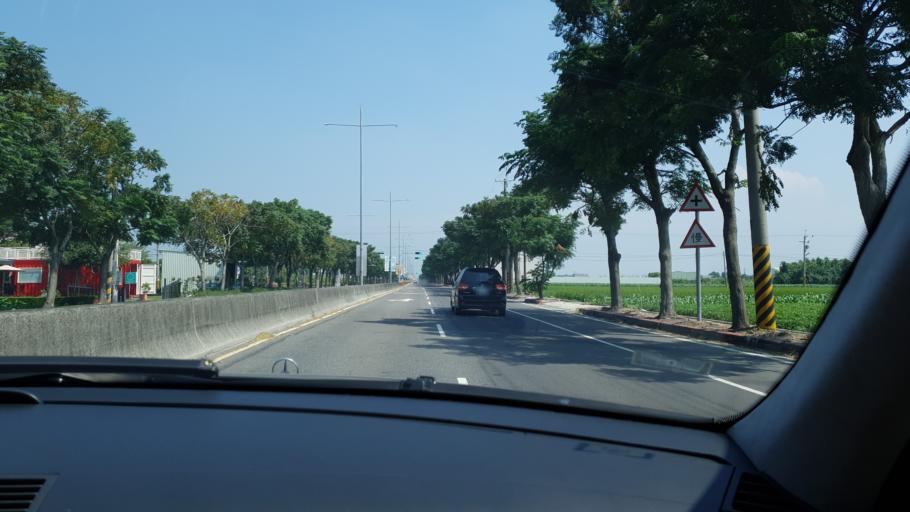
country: TW
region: Taiwan
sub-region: Yunlin
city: Douliu
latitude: 23.7356
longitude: 120.4429
